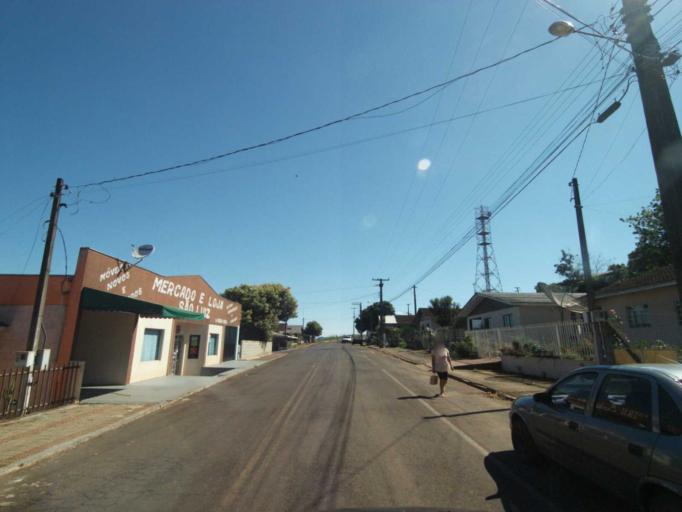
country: BR
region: Parana
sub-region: Coronel Vivida
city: Coronel Vivida
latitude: -25.9581
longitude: -52.8098
